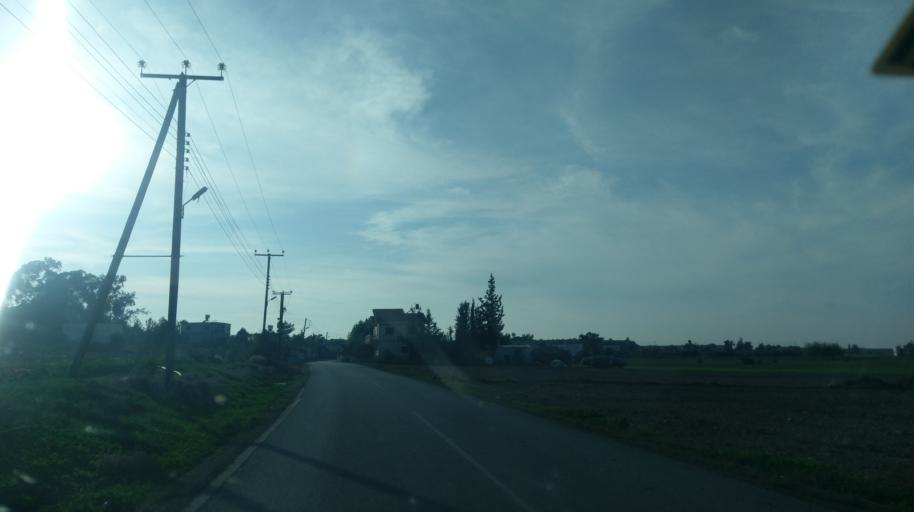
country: CY
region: Ammochostos
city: Achna
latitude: 35.0978
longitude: 33.7994
